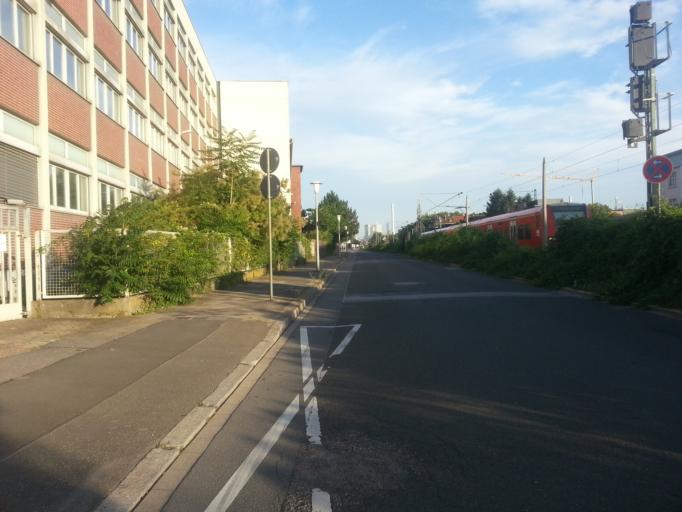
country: DE
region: Baden-Wuerttemberg
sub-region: Karlsruhe Region
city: Mannheim
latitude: 49.4672
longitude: 8.4893
